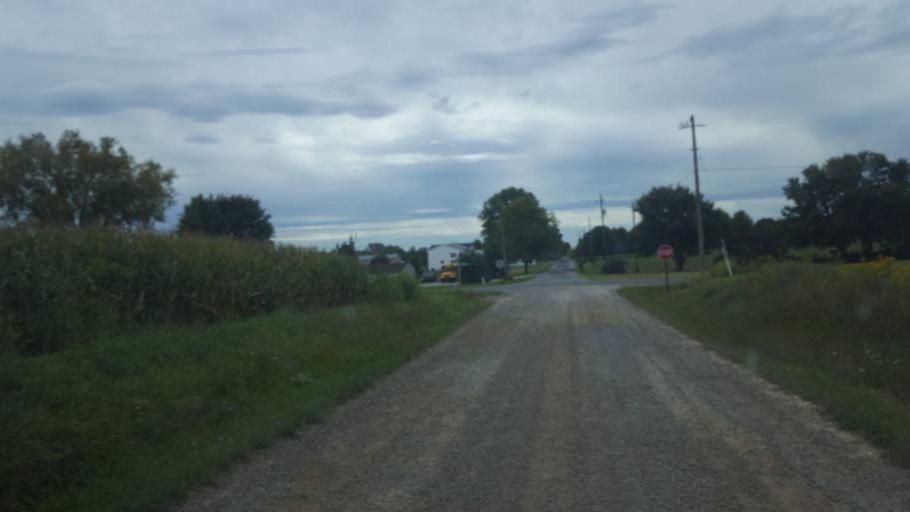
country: US
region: Ohio
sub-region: Knox County
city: Centerburg
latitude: 40.3216
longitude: -82.7177
